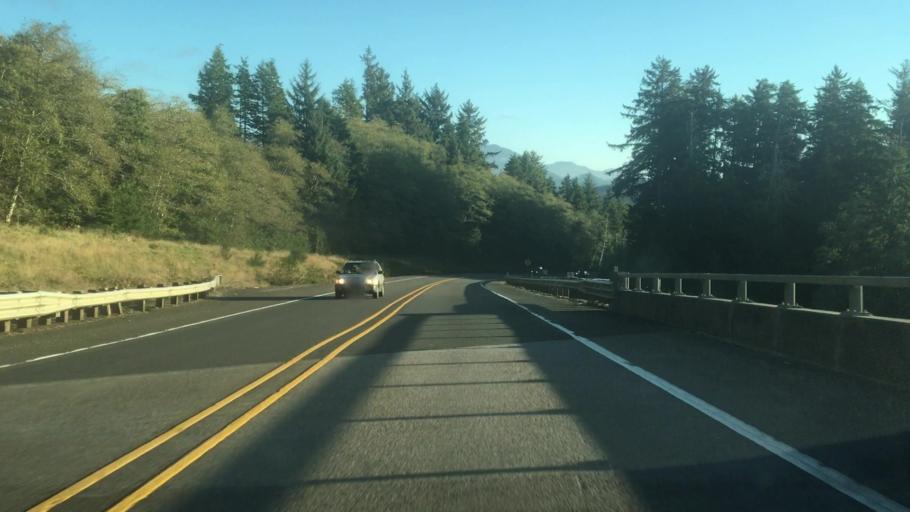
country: US
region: Oregon
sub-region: Clatsop County
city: Cannon Beach
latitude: 45.9039
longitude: -123.9536
